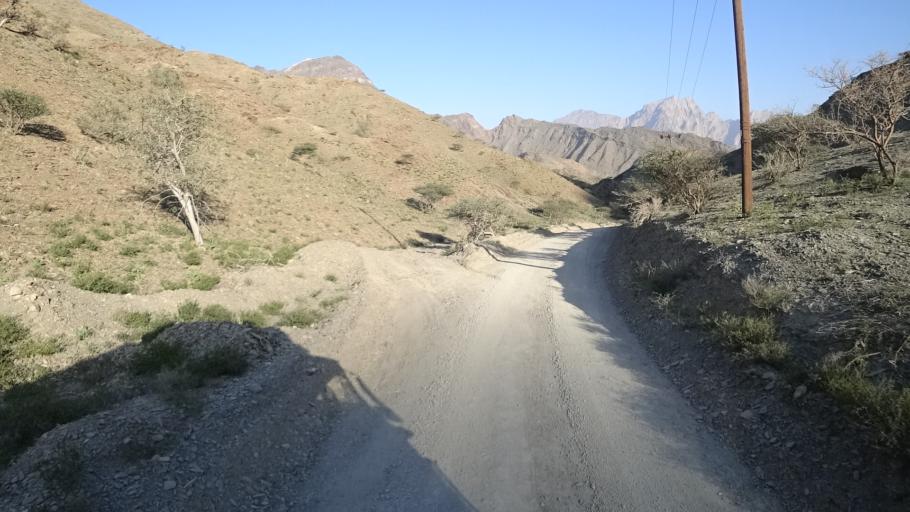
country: OM
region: Al Batinah
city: Rustaq
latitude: 23.2726
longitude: 57.3818
